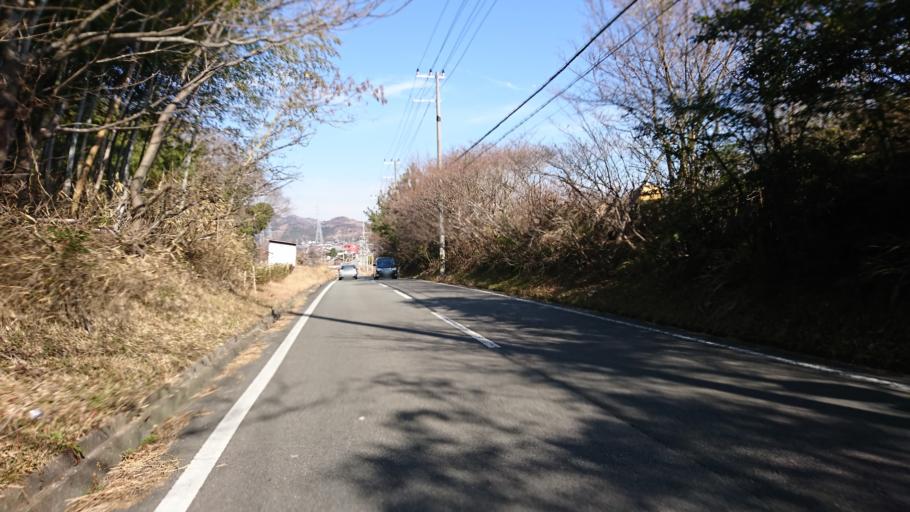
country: JP
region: Hyogo
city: Kakogawacho-honmachi
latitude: 34.8005
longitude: 134.8581
